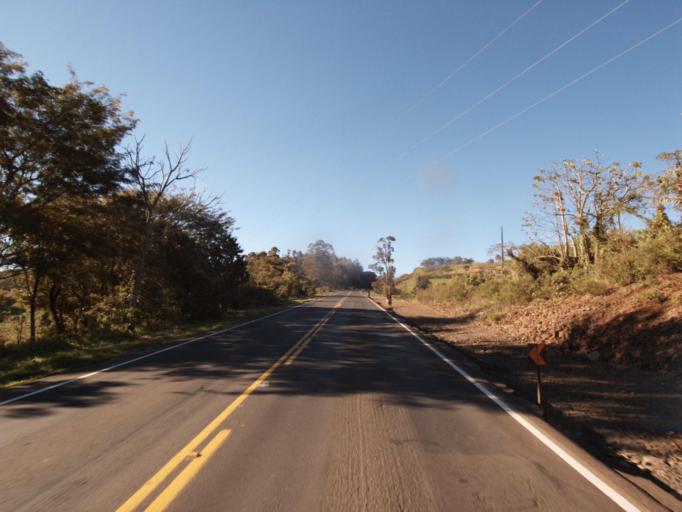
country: AR
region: Misiones
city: Bernardo de Irigoyen
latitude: -26.5006
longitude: -53.5072
